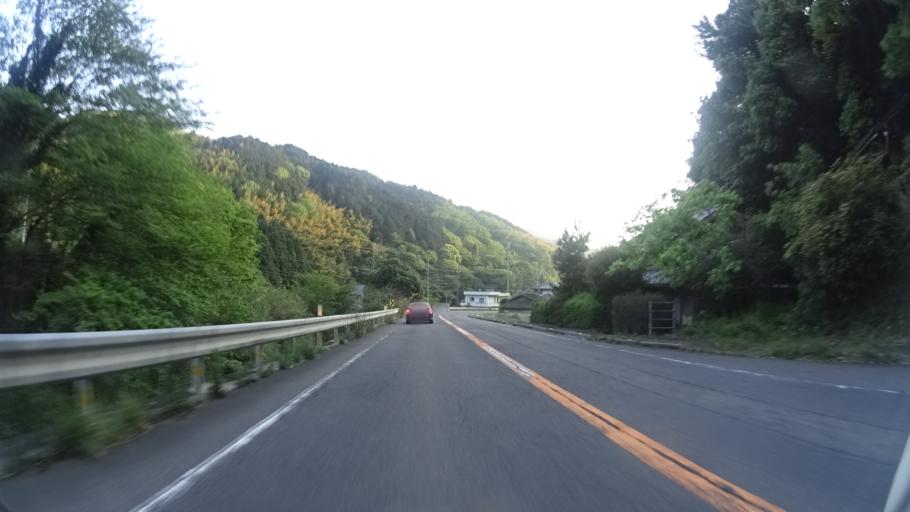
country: JP
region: Ehime
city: Kawanoecho
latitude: 33.9921
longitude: 133.6427
